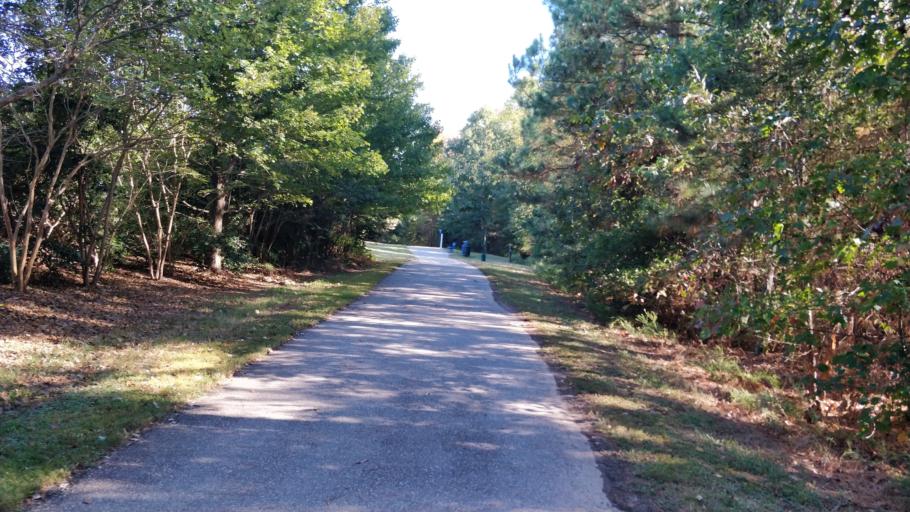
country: US
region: North Carolina
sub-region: Wake County
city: Morrisville
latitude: 35.8294
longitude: -78.8412
